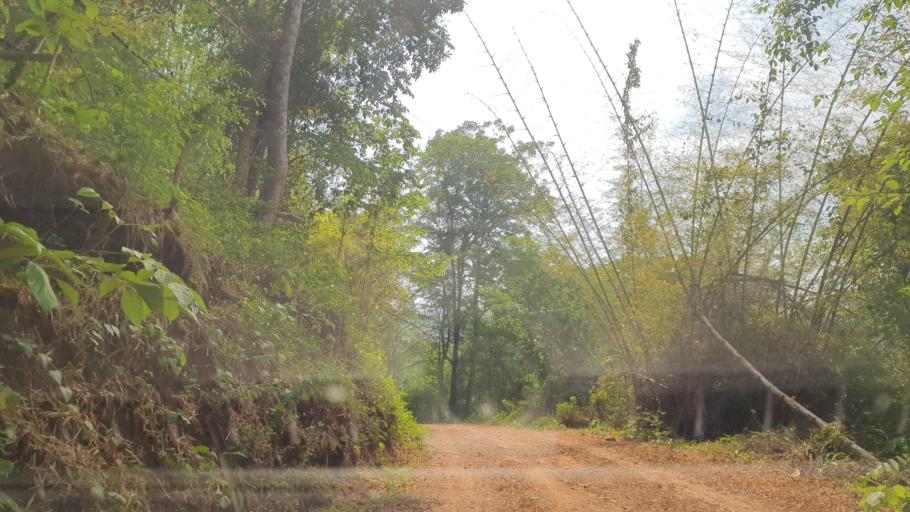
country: TH
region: Chiang Mai
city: Samoeng
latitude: 18.7973
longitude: 98.7955
